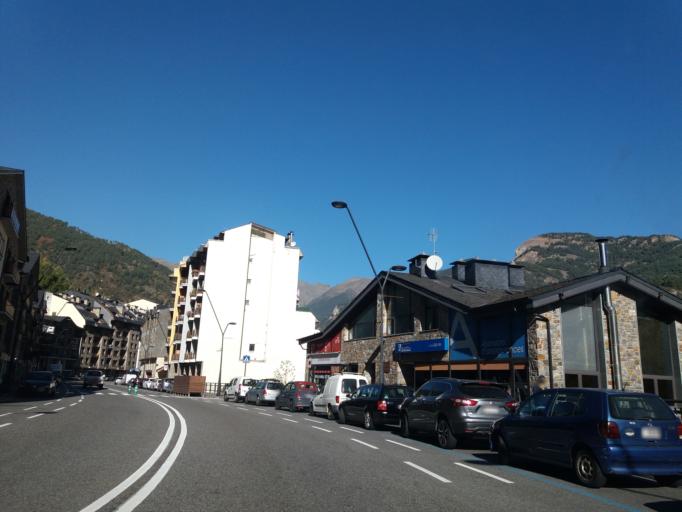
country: AD
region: La Massana
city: la Massana
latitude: 42.5411
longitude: 1.5192
